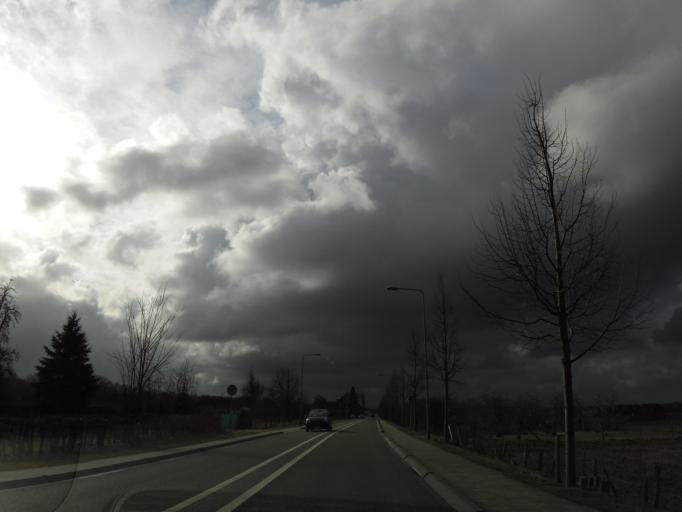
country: NL
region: Limburg
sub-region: Eijsden-Margraten
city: Eijsden
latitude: 50.7815
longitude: 5.7269
